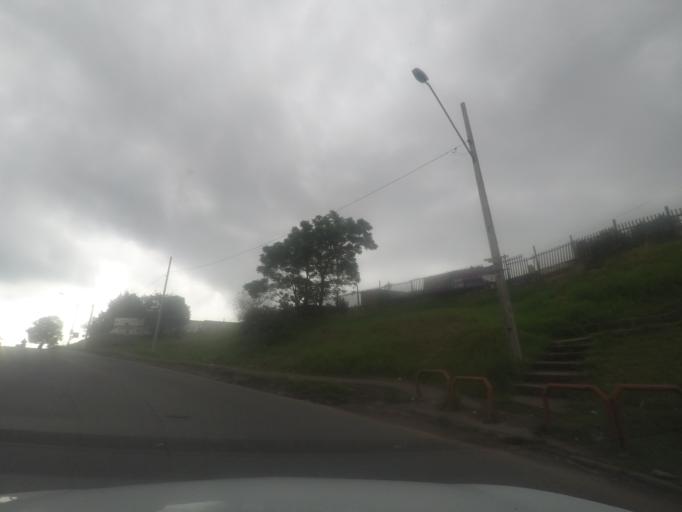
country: BR
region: Parana
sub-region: Sao Jose Dos Pinhais
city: Sao Jose dos Pinhais
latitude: -25.5535
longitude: -49.2759
